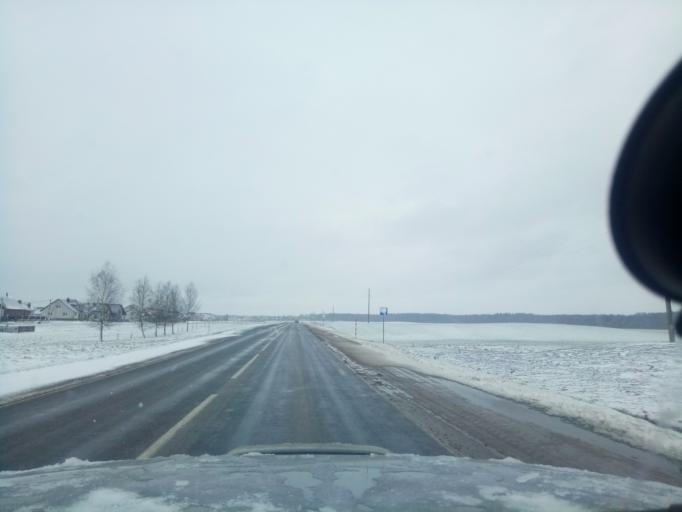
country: BY
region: Minsk
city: Nyasvizh
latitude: 53.2211
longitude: 26.6483
